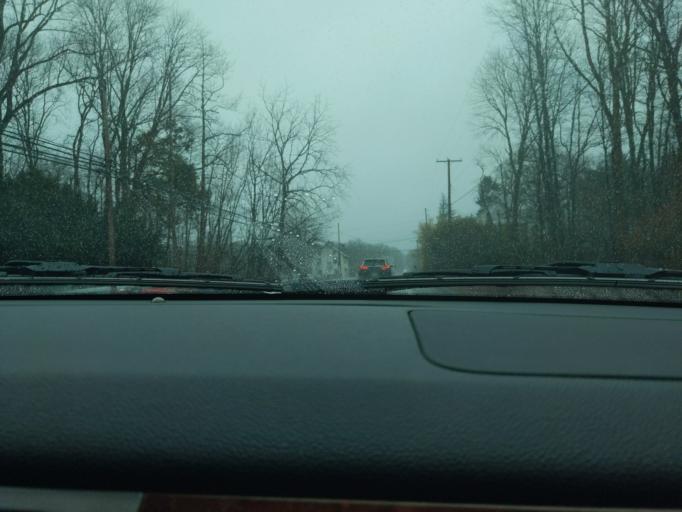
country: US
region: Pennsylvania
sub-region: Bucks County
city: Richlandtown
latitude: 40.4322
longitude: -75.2989
